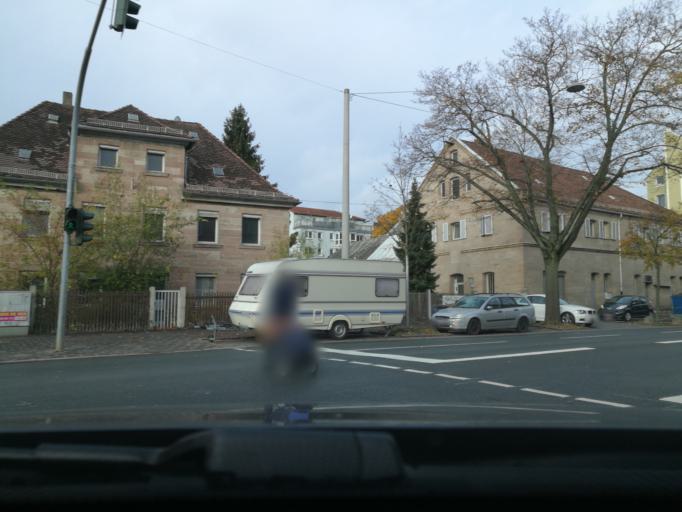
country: DE
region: Bavaria
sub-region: Regierungsbezirk Mittelfranken
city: Furth
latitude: 49.4839
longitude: 10.9975
